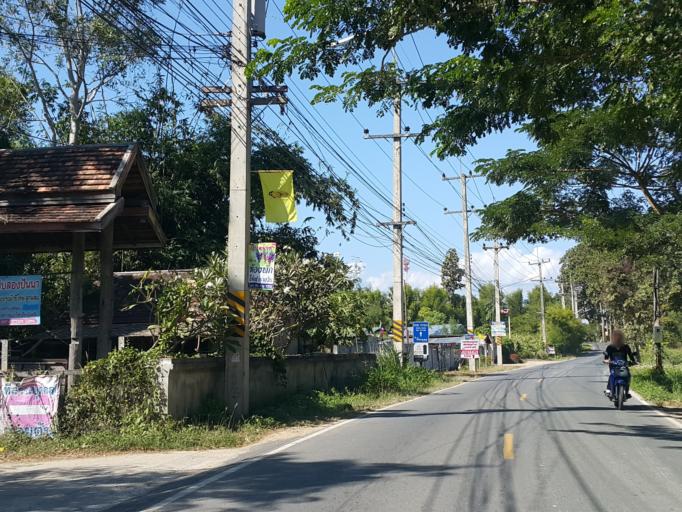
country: TH
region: Chiang Mai
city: San Sai
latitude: 18.9542
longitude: 98.9236
